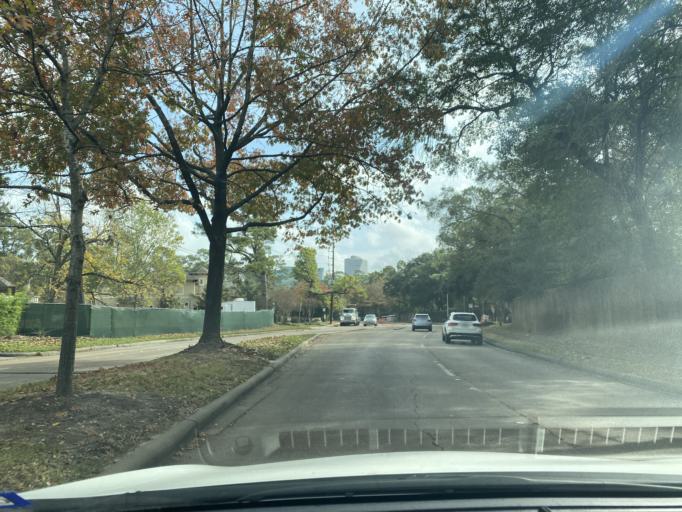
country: US
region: Texas
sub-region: Harris County
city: Hunters Creek Village
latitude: 29.7638
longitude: -95.4718
